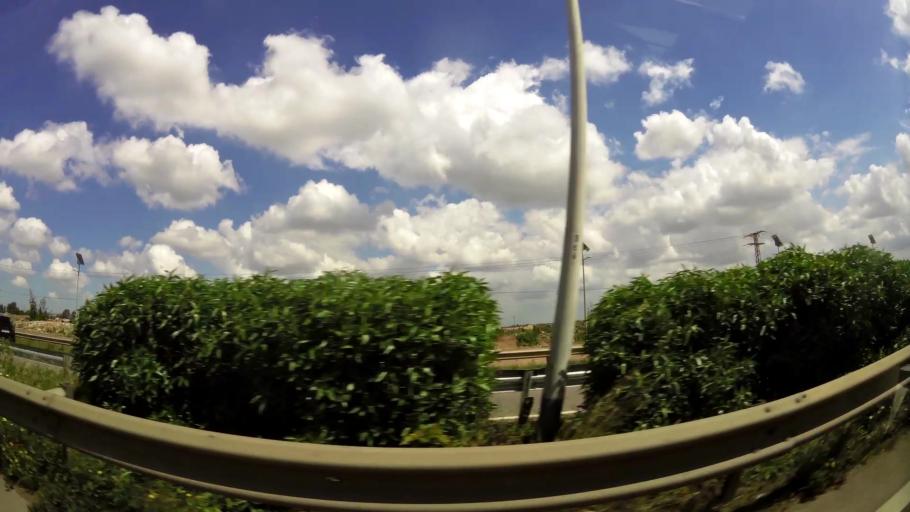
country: MA
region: Chaouia-Ouardigha
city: Nouaseur
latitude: 33.4148
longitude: -7.6265
